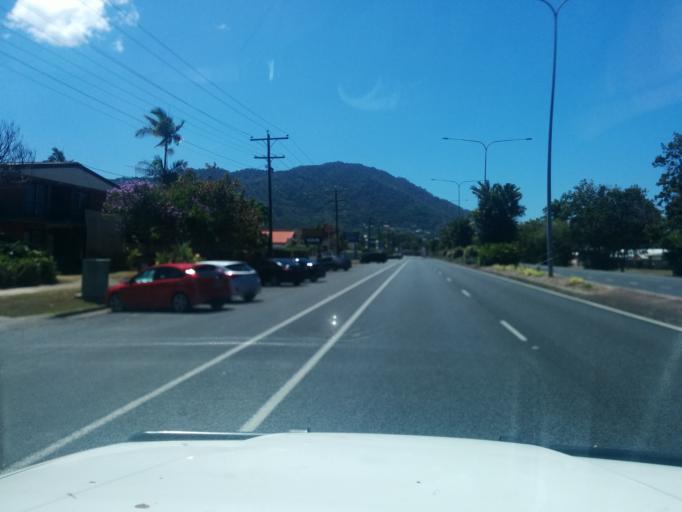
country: AU
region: Queensland
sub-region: Cairns
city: Woree
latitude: -16.9501
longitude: 145.7423
